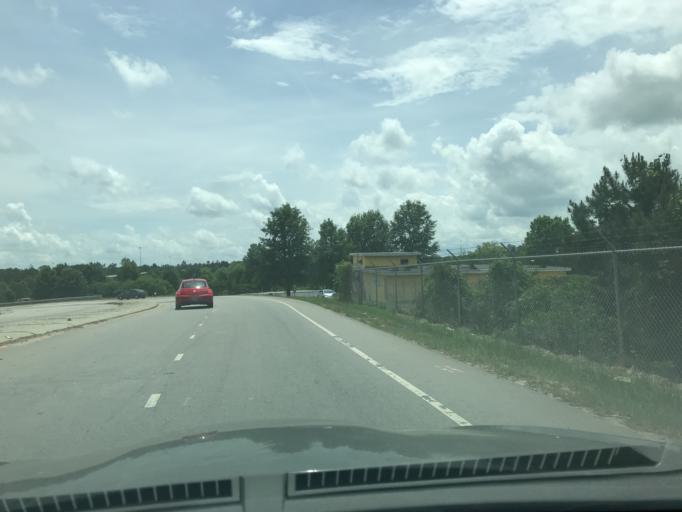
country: US
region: North Carolina
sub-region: Wake County
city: Wake Forest
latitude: 35.8815
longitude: -78.5743
